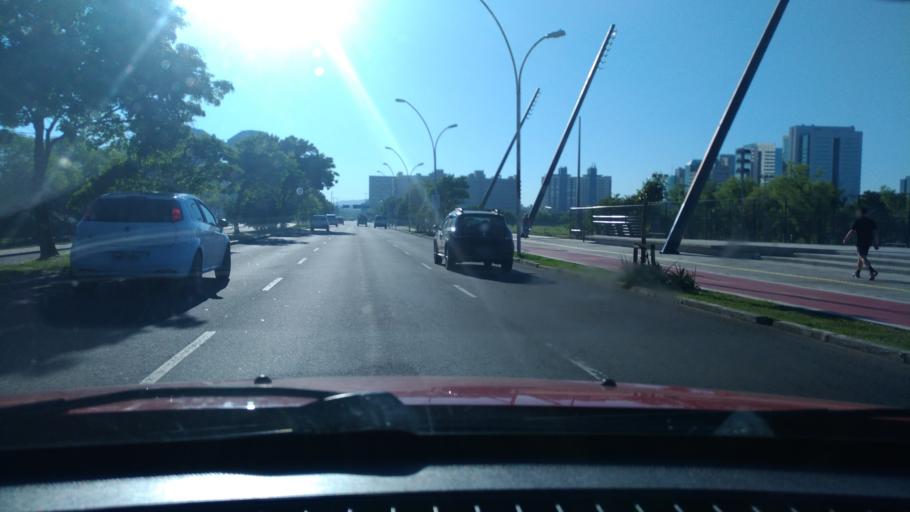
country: BR
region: Rio Grande do Sul
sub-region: Porto Alegre
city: Porto Alegre
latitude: -30.0424
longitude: -51.2371
